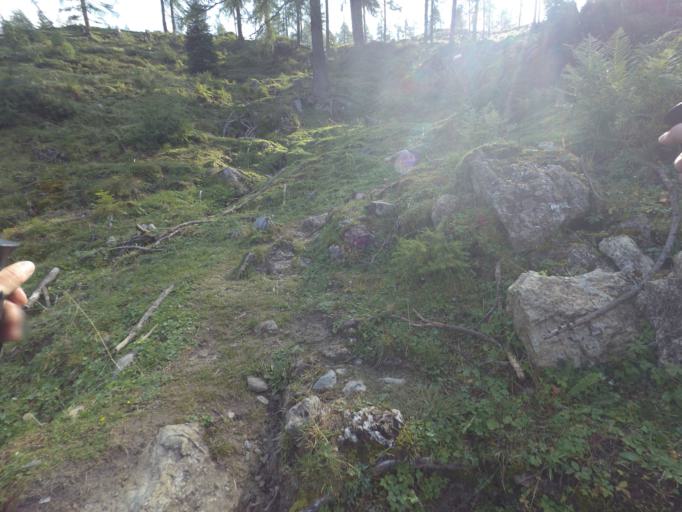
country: AT
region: Salzburg
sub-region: Politischer Bezirk Sankt Johann im Pongau
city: Kleinarl
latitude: 47.2631
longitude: 13.2696
